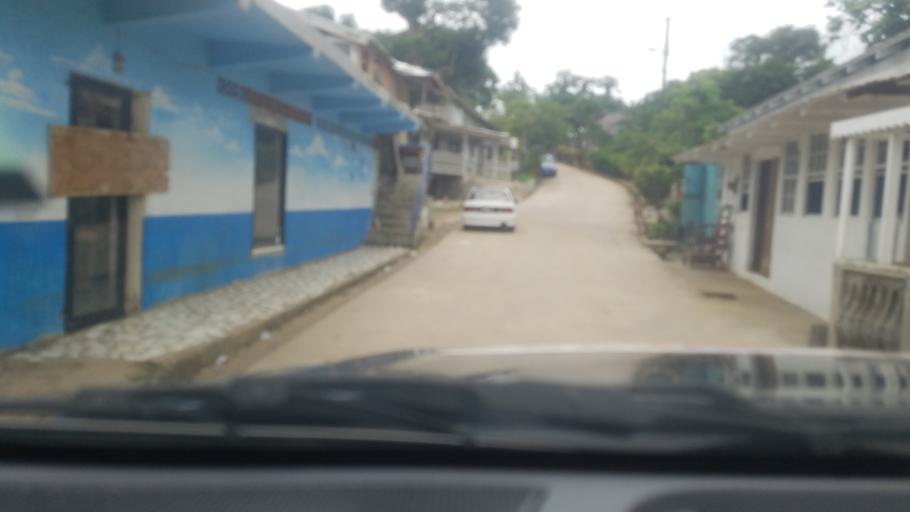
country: LC
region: Micoud Quarter
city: Micoud
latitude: 13.8047
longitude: -60.9472
